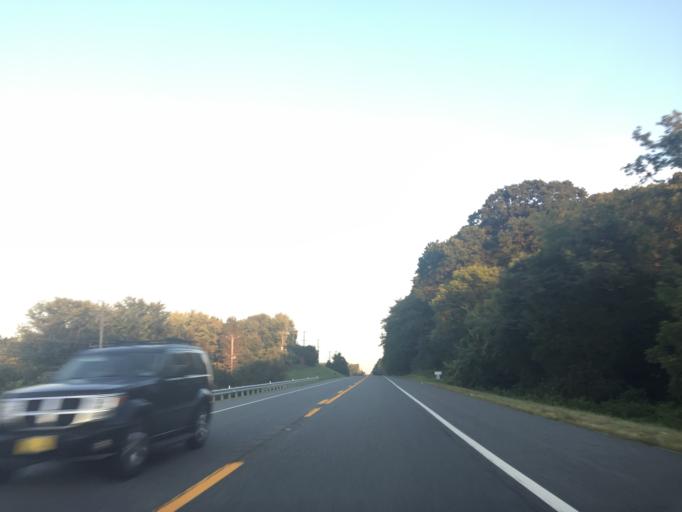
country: US
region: Pennsylvania
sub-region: York County
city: Susquehanna Trails
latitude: 39.6999
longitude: -76.3289
